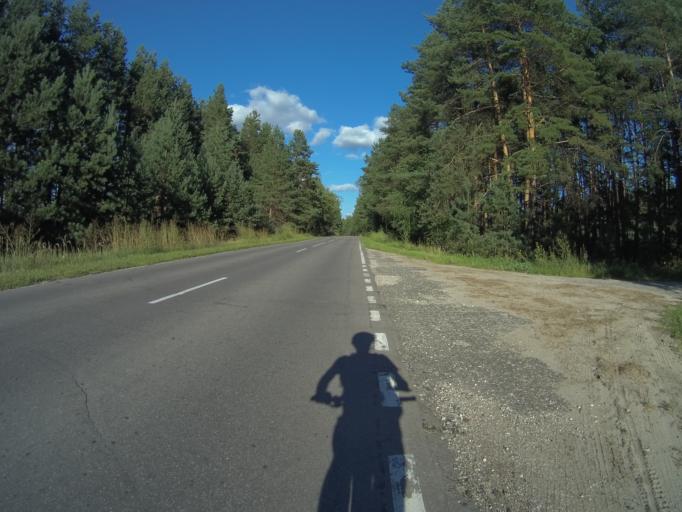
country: RU
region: Vladimir
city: Gusevskiy
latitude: 55.5753
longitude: 40.5086
